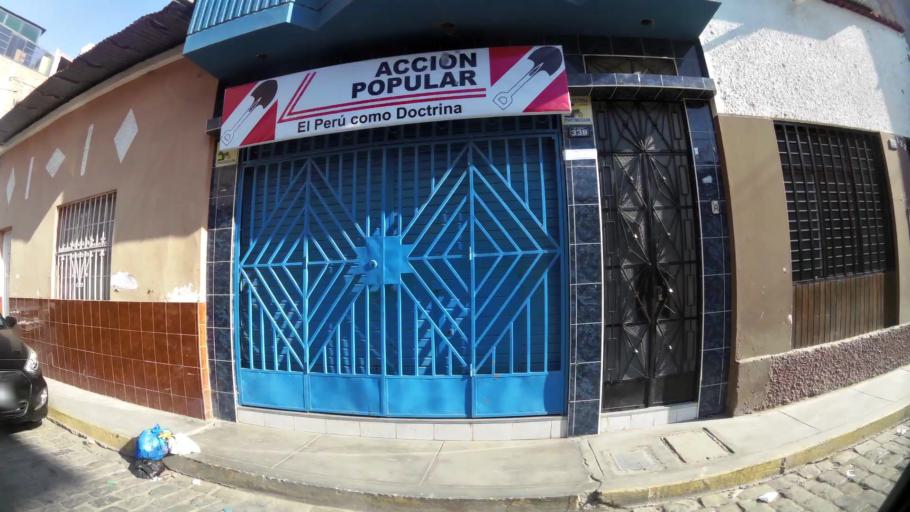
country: PE
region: Lambayeque
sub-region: Provincia de Chiclayo
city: Chiclayo
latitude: -6.7742
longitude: -79.8405
